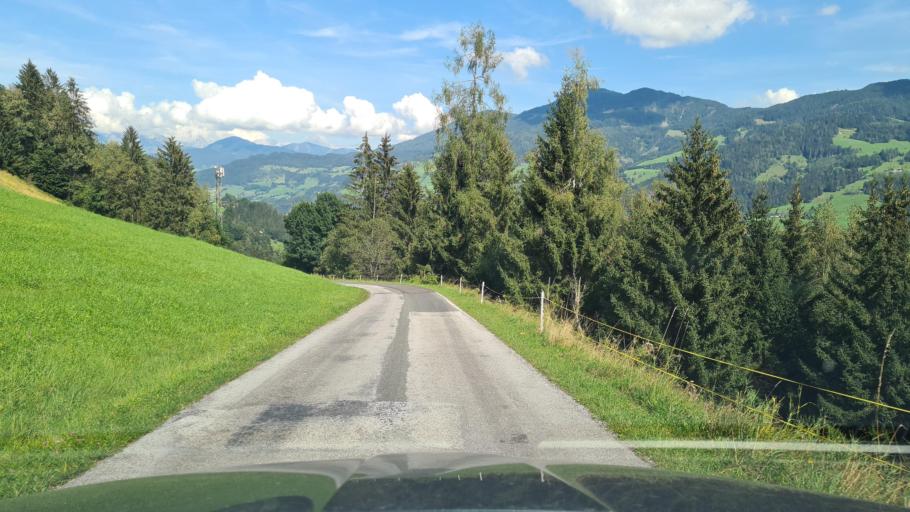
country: AT
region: Salzburg
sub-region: Politischer Bezirk Sankt Johann im Pongau
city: Sankt Johann im Pongau
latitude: 47.3548
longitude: 13.1853
